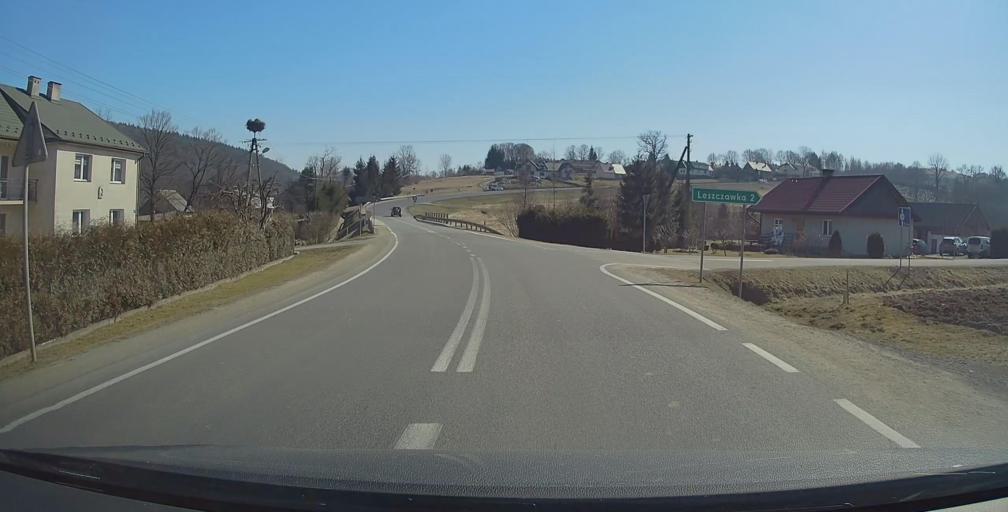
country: PL
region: Subcarpathian Voivodeship
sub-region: Powiat przemyski
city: Bircza
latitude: 49.6634
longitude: 22.4329
